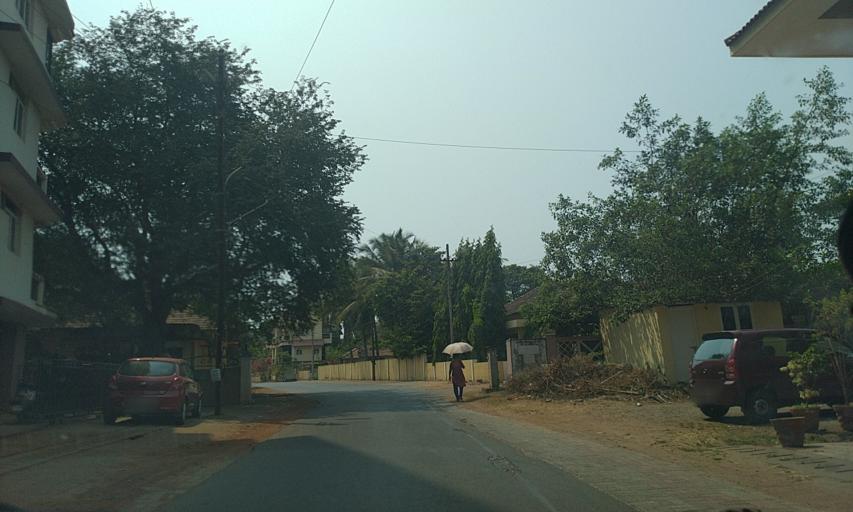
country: IN
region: Goa
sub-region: North Goa
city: Taleigao
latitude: 15.4724
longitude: 73.8098
